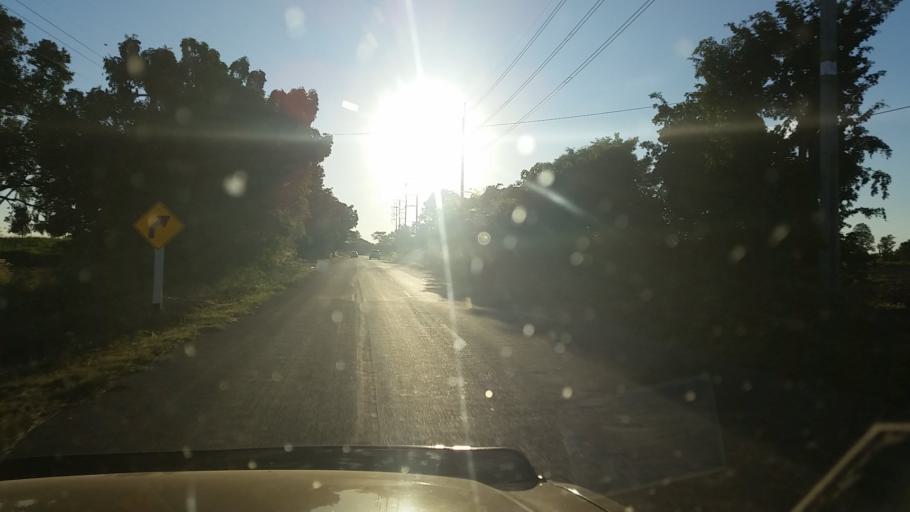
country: TH
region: Chaiyaphum
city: Sap Yai
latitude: 15.6599
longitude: 101.6587
